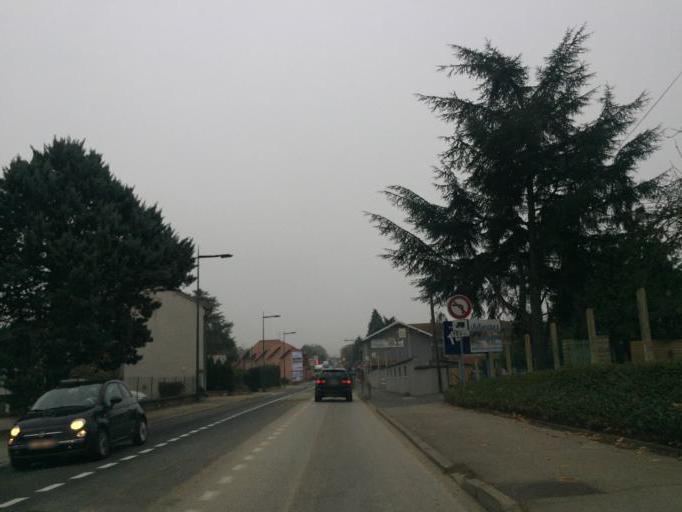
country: FR
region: Rhone-Alpes
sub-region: Departement de l'Ain
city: Mionnay
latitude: 45.8740
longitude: 4.9114
